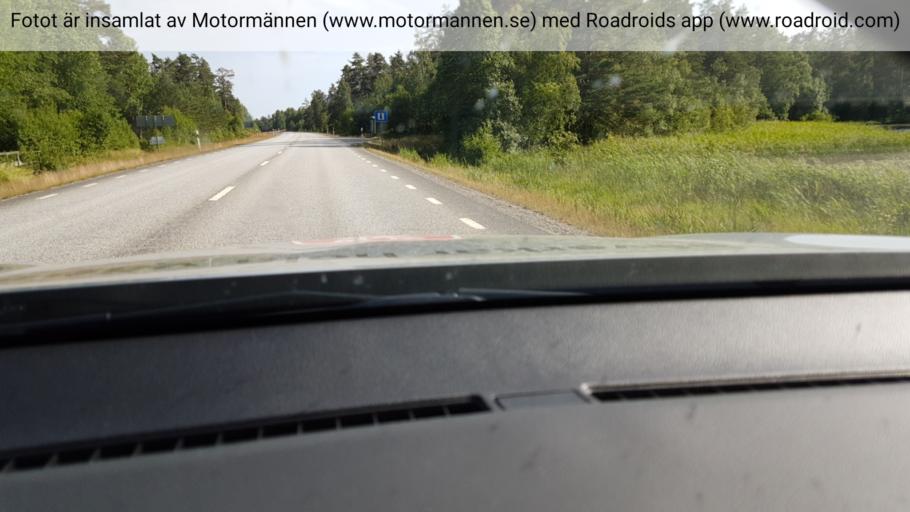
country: SE
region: Joenkoeping
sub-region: Eksjo Kommun
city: Eksjoe
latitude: 57.6743
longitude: 14.9529
